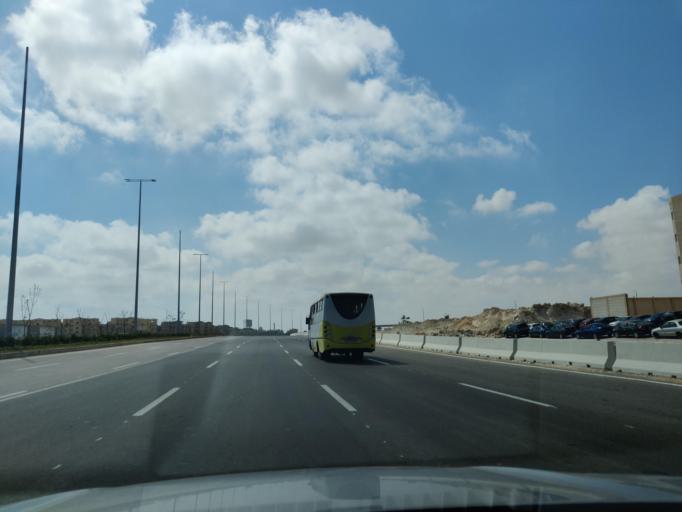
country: EG
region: Muhafazat Matruh
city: Al `Alamayn
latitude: 30.9573
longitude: 28.7631
